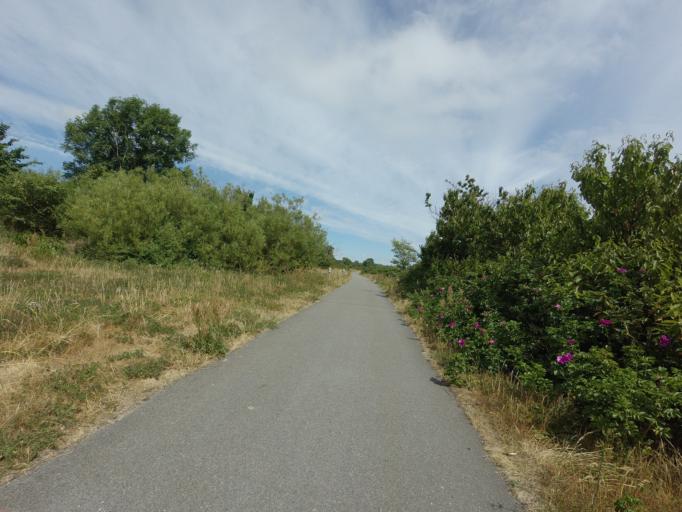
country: SE
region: Skane
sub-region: Simrishamns Kommun
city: Simrishamn
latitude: 55.5219
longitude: 14.3474
